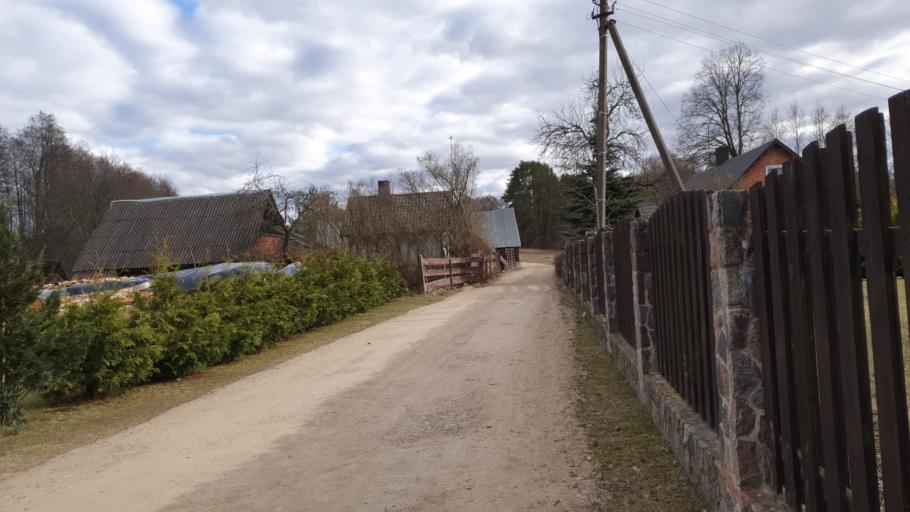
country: LT
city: Grigiskes
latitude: 54.7351
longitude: 25.0266
